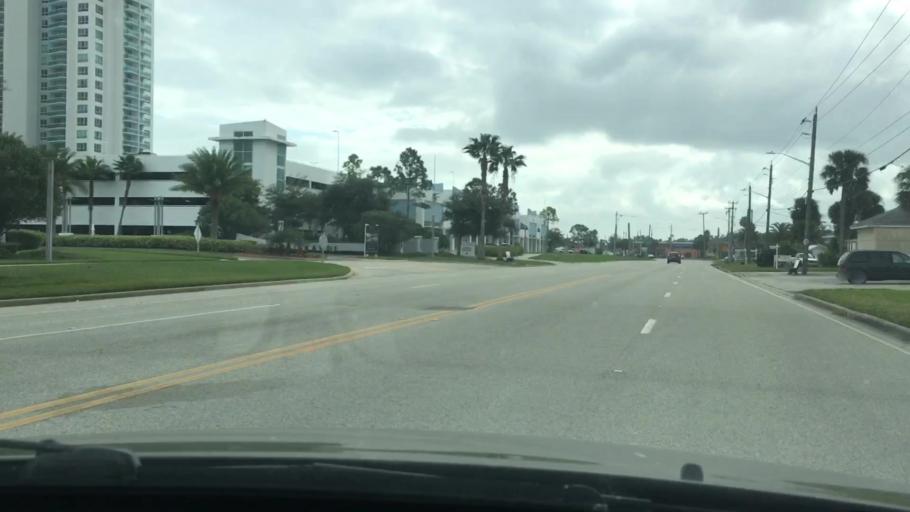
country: US
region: Florida
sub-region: Volusia County
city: Holly Hill
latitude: 29.2330
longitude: -81.0296
